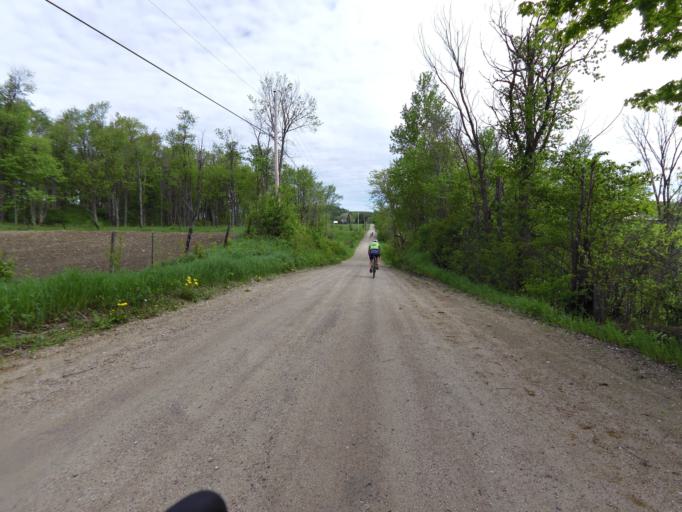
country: CA
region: Quebec
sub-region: Outaouais
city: Wakefield
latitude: 45.7353
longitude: -75.8898
